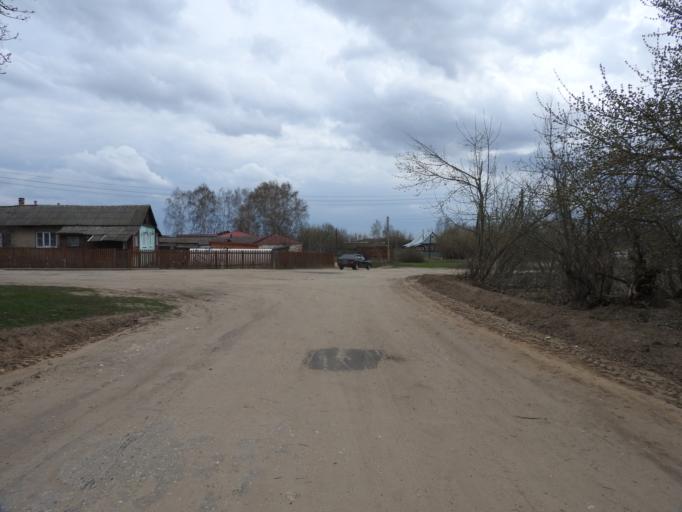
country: RU
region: Rjazan
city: Shilovo
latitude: 54.3772
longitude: 40.7634
